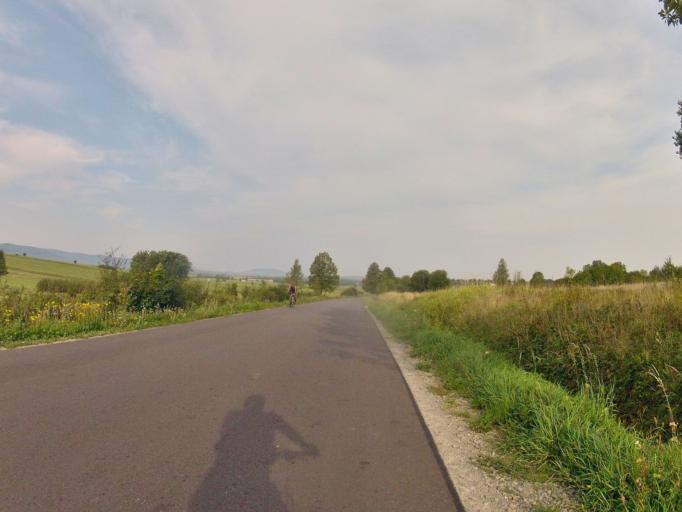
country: PL
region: Subcarpathian Voivodeship
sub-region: Powiat jasielski
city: Osiek Jasielski
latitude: 49.6256
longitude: 21.5075
